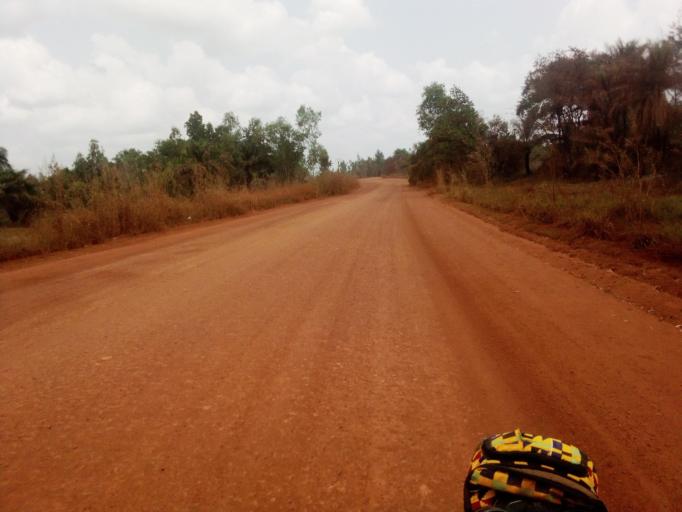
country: SL
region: Southern Province
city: Mogbwemo
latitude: 7.7524
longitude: -12.2939
